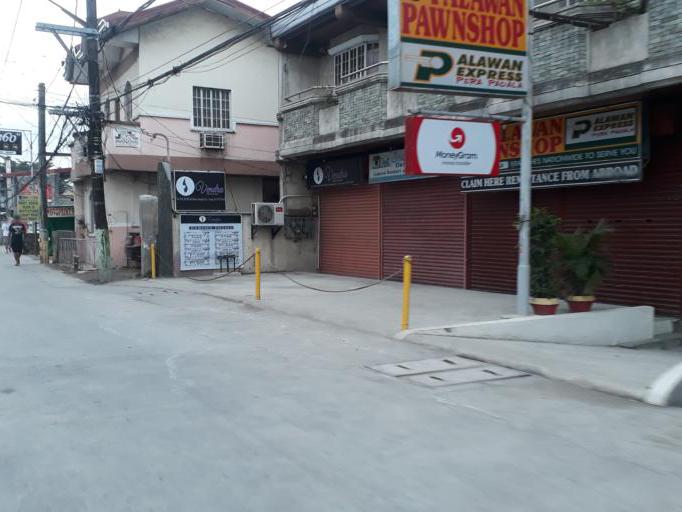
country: PH
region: Central Luzon
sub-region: Province of Bulacan
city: Obando
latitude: 14.7068
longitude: 120.9466
